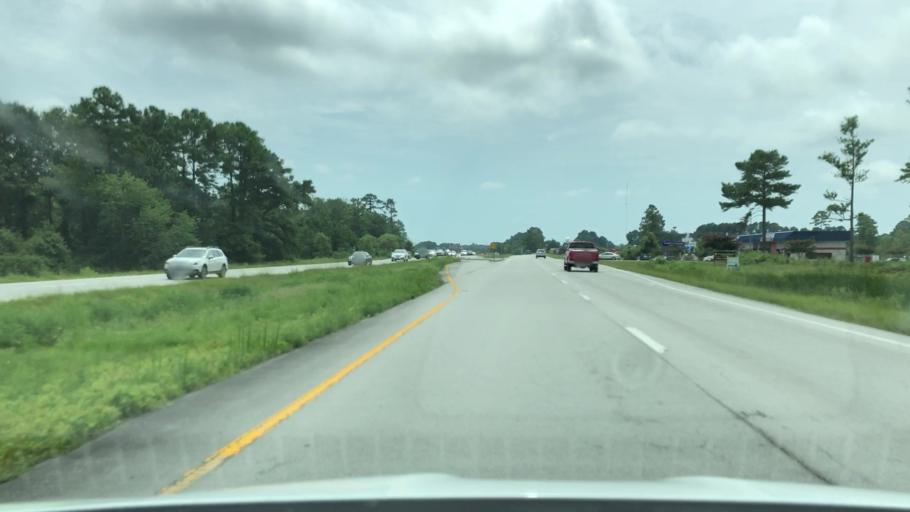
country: US
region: North Carolina
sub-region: Carteret County
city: Newport
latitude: 34.7946
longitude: -76.8775
